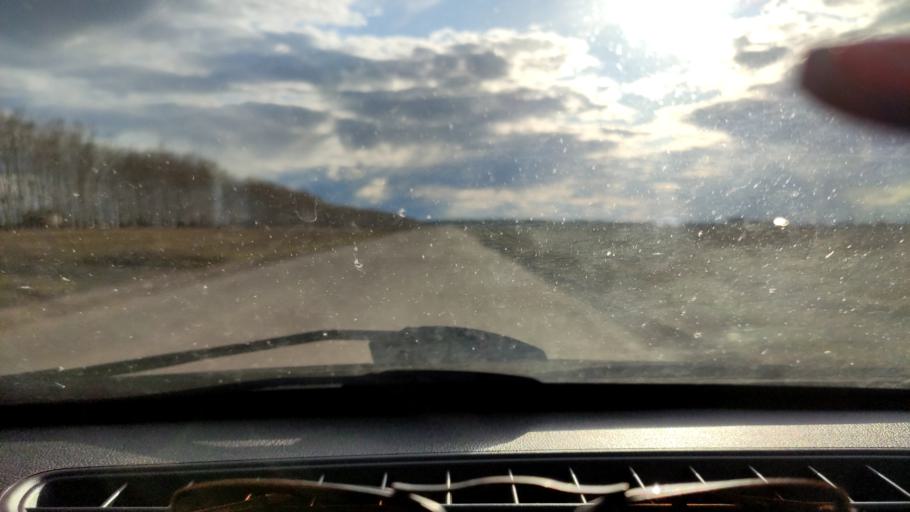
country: RU
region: Bashkortostan
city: Karmaskaly
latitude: 54.3503
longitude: 56.1267
